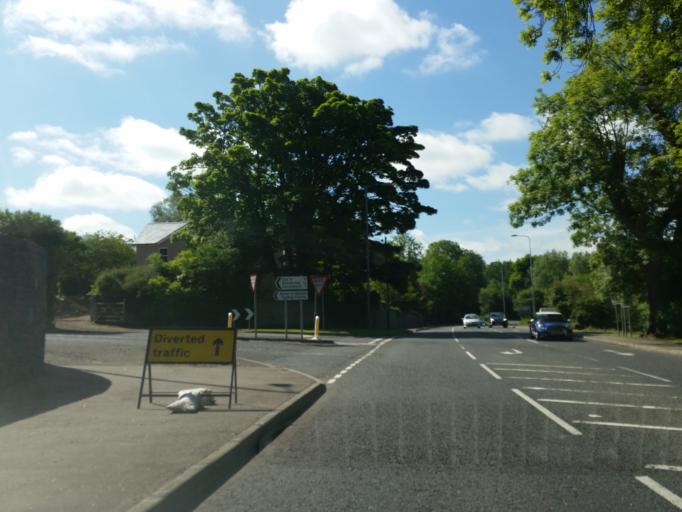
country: GB
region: Northern Ireland
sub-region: Fermanagh District
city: Enniskillen
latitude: 54.3541
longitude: -7.6247
